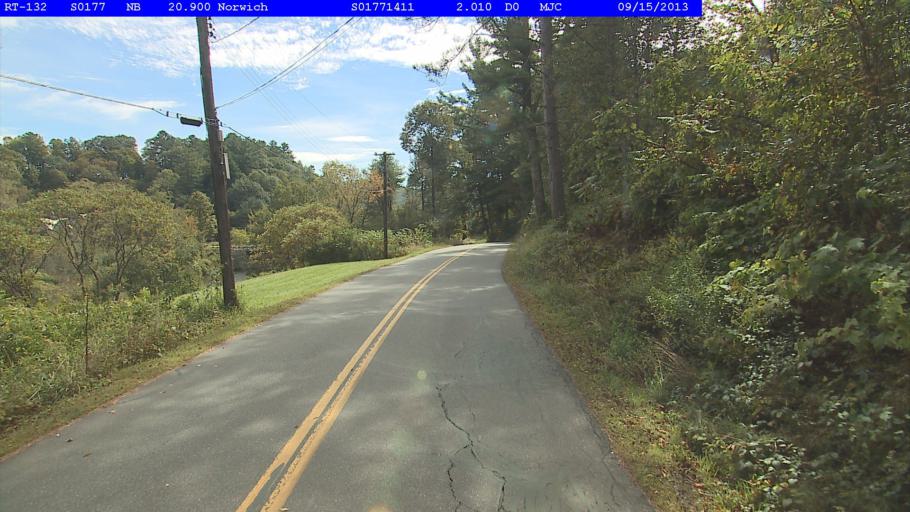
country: US
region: New Hampshire
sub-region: Grafton County
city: Hanover
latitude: 43.7638
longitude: -72.2411
